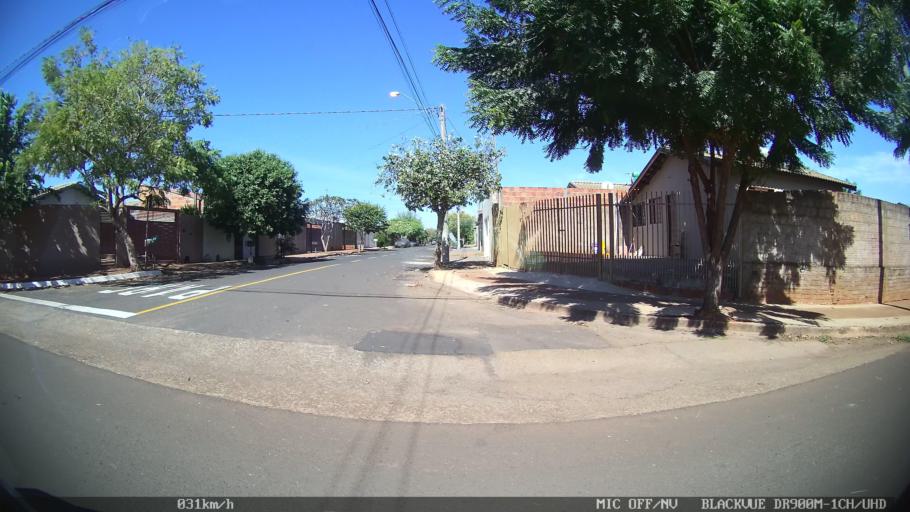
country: BR
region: Sao Paulo
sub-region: Sao Jose Do Rio Preto
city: Sao Jose do Rio Preto
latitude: -20.7406
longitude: -49.4183
